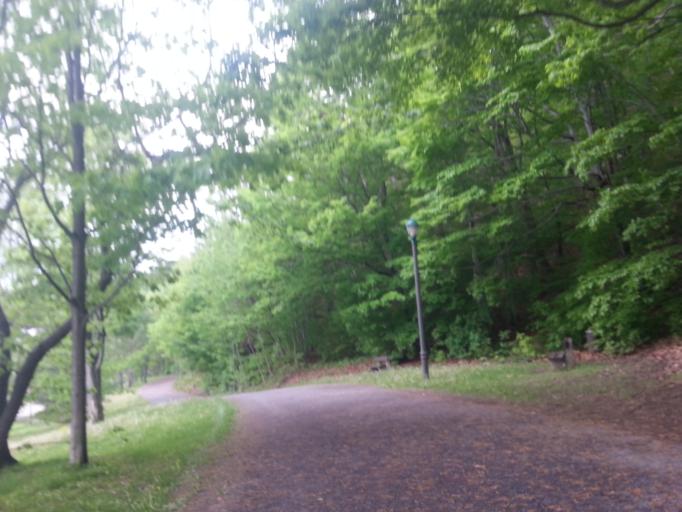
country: CA
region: Quebec
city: L'Ancienne-Lorette
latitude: 46.7502
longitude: -71.3186
